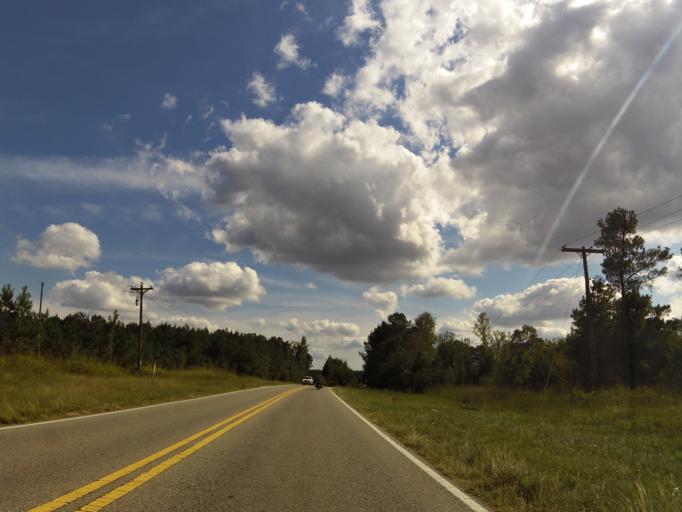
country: US
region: Alabama
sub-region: Dallas County
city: Selmont-West Selmont
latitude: 32.3073
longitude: -86.9842
